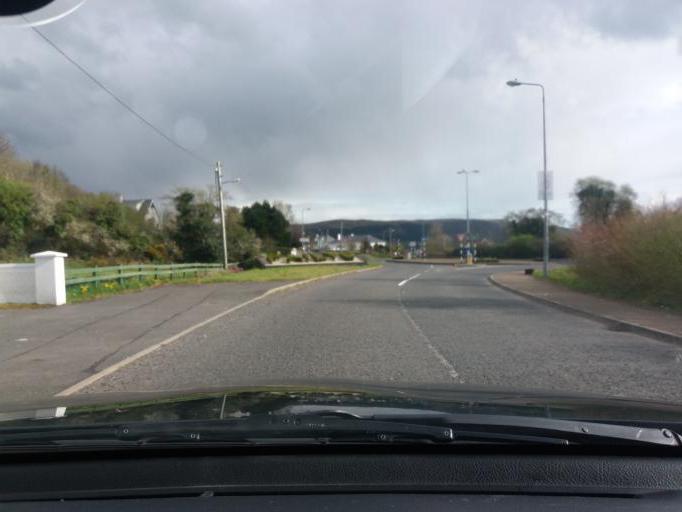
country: IE
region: Connaught
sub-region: County Leitrim
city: Manorhamilton
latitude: 54.3092
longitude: -8.1844
